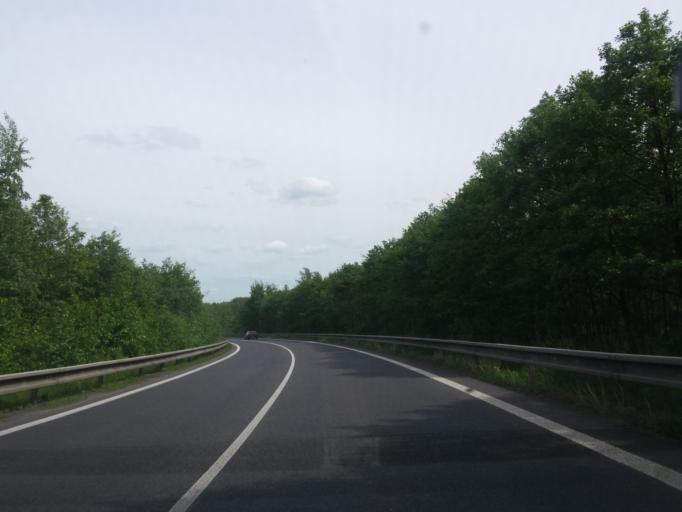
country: CZ
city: Novy Bor
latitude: 50.7517
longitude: 14.5371
